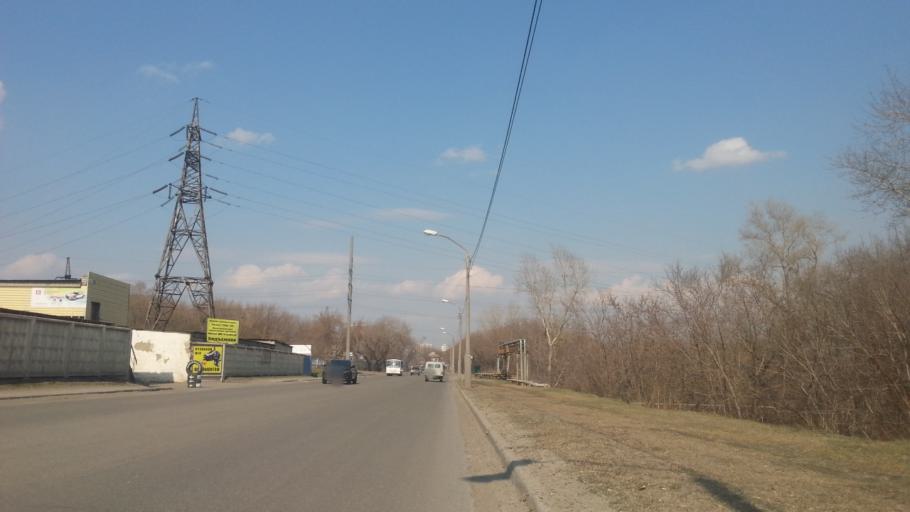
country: RU
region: Altai Krai
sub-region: Gorod Barnaulskiy
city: Barnaul
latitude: 53.3191
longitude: 83.7618
